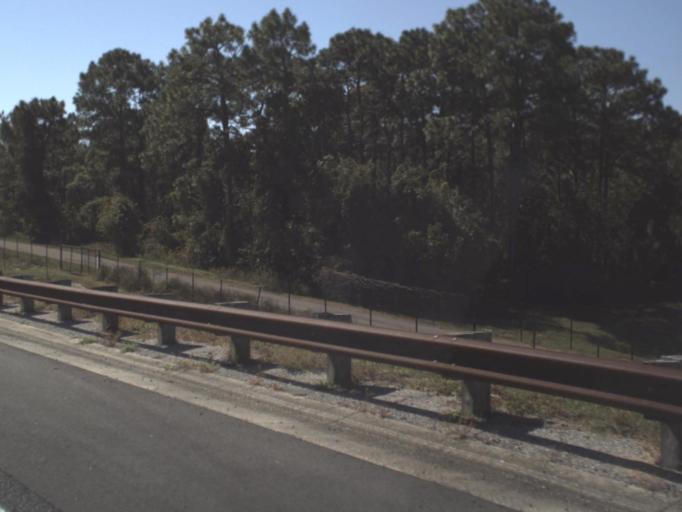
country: US
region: Florida
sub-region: Hernando County
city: Brookridge
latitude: 28.6079
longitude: -82.4935
